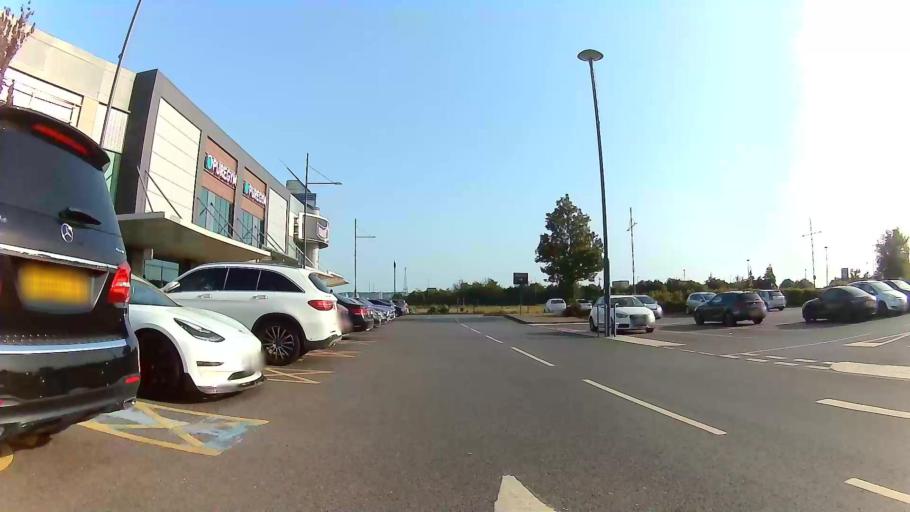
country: GB
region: England
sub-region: Greater London
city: Barking
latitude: 51.5163
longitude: 0.0820
